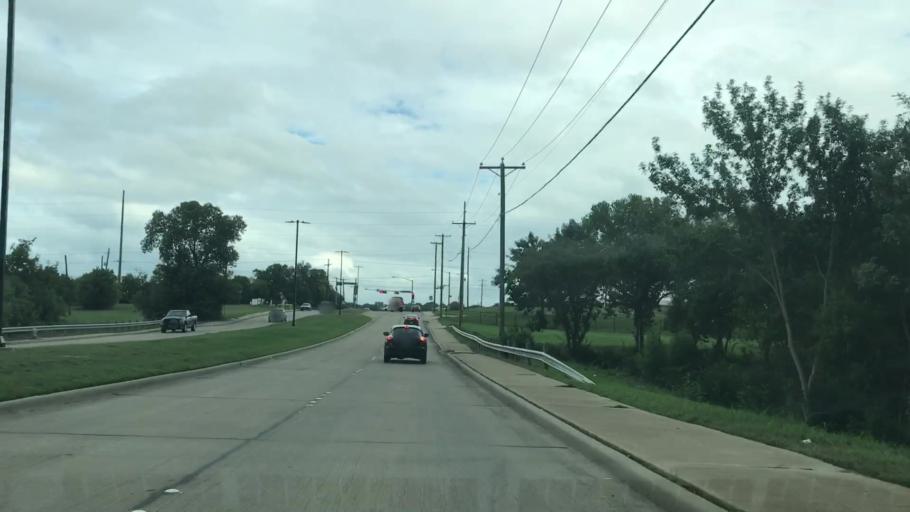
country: US
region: Texas
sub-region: Dallas County
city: Garland
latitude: 32.8883
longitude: -96.6129
